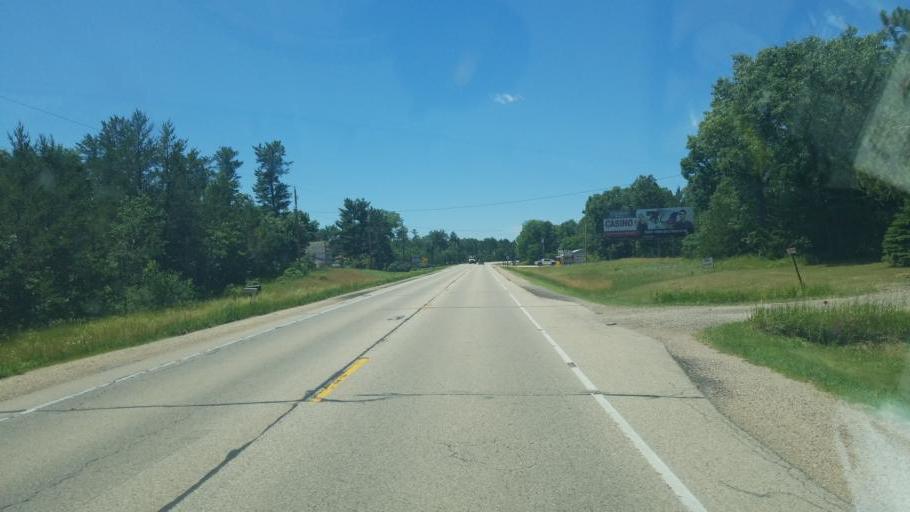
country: US
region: Wisconsin
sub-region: Juneau County
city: New Lisbon
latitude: 44.0313
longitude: -90.0479
